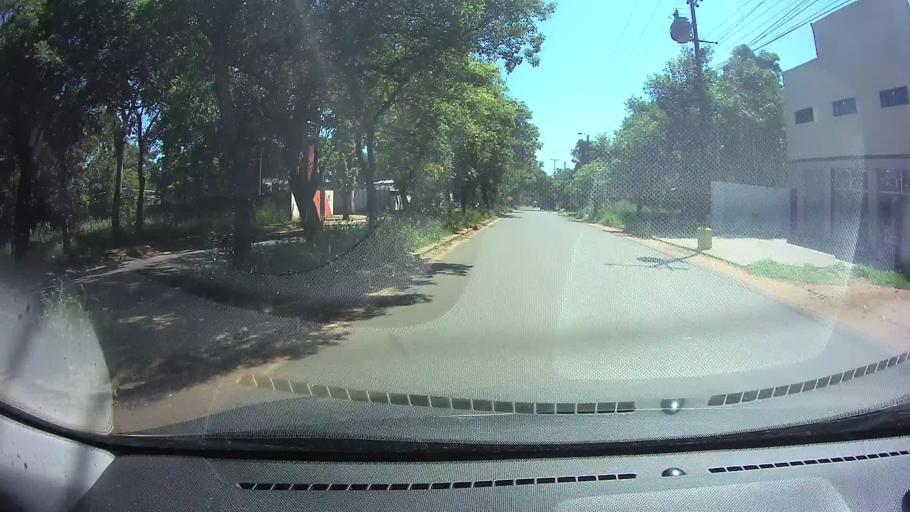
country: PY
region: Central
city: Fernando de la Mora
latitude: -25.2935
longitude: -57.5222
